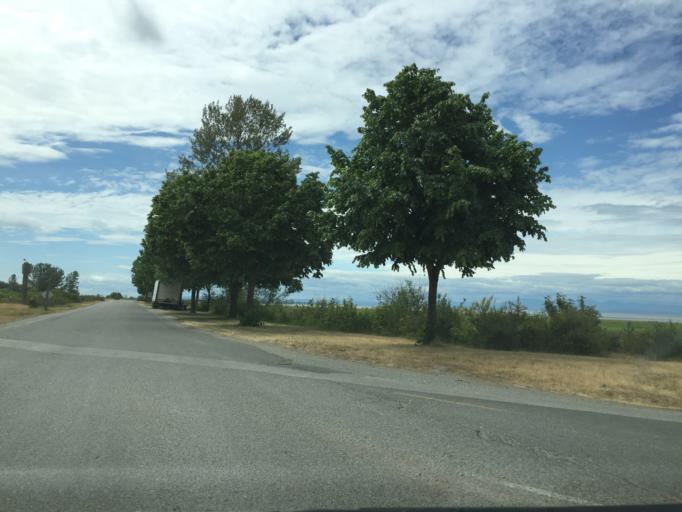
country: CA
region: British Columbia
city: Richmond
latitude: 49.2159
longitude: -123.2012
